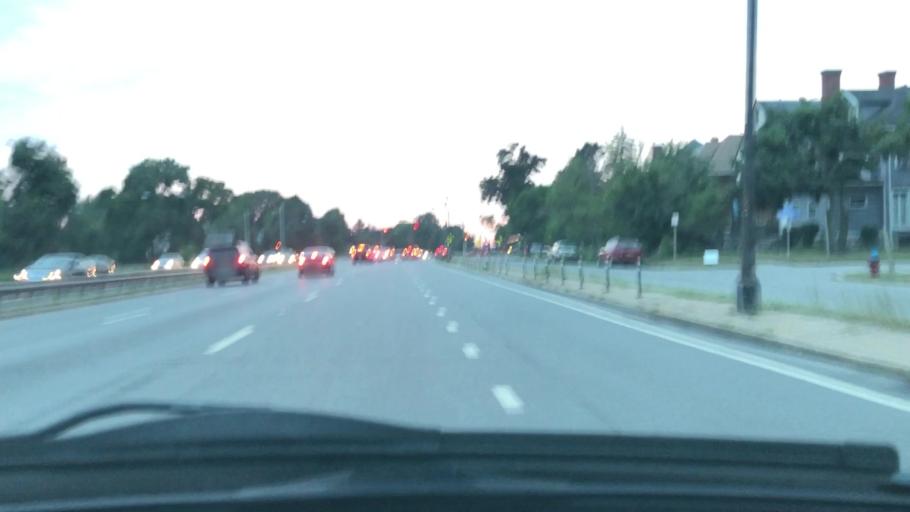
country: US
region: New York
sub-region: Erie County
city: Kenmore
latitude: 42.9294
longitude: -78.8532
